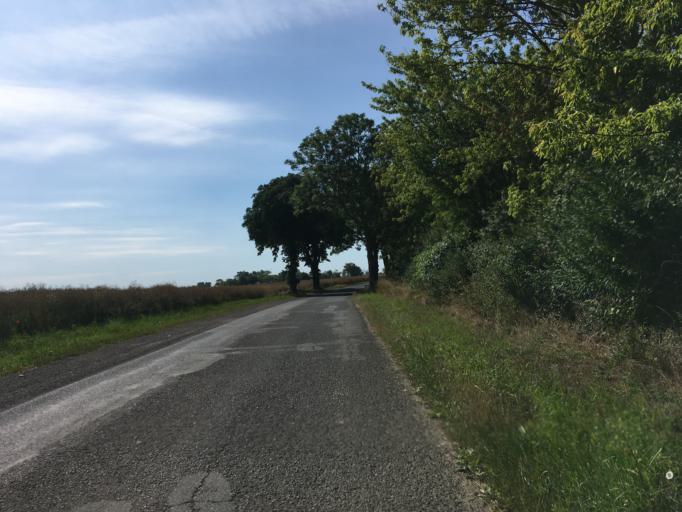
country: DE
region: Brandenburg
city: Gramzow
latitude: 53.2885
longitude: 14.0469
